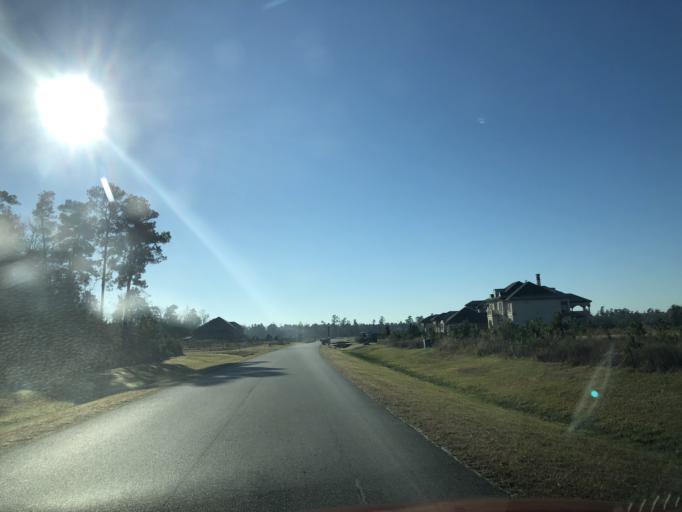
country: US
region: Texas
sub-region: Montgomery County
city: Porter Heights
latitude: 30.0776
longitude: -95.3199
